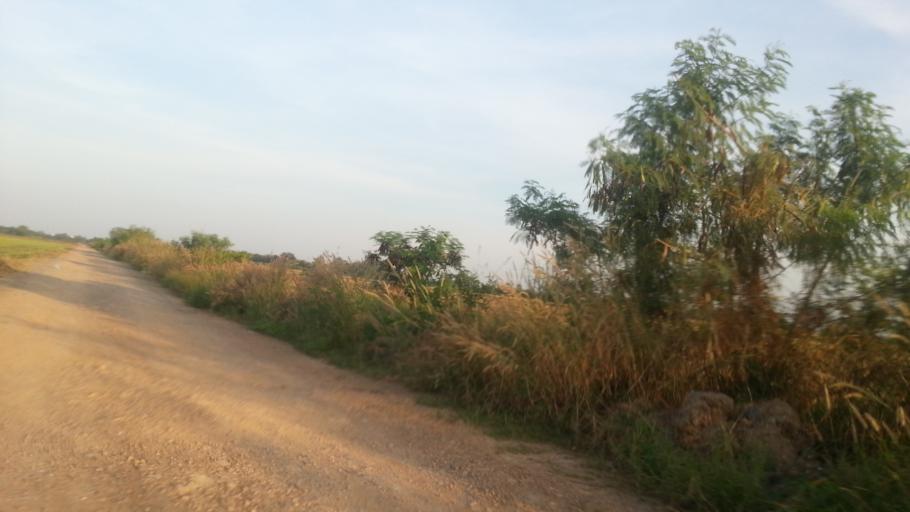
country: TH
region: Pathum Thani
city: Ban Lam Luk Ka
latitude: 14.0353
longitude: 100.8511
